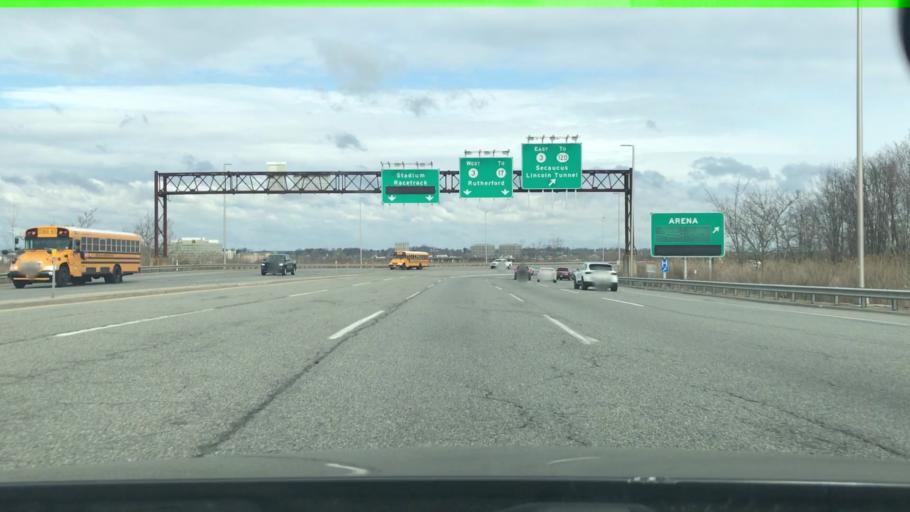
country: US
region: New Jersey
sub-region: Hudson County
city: Secaucus
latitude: 40.8043
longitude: -74.0799
